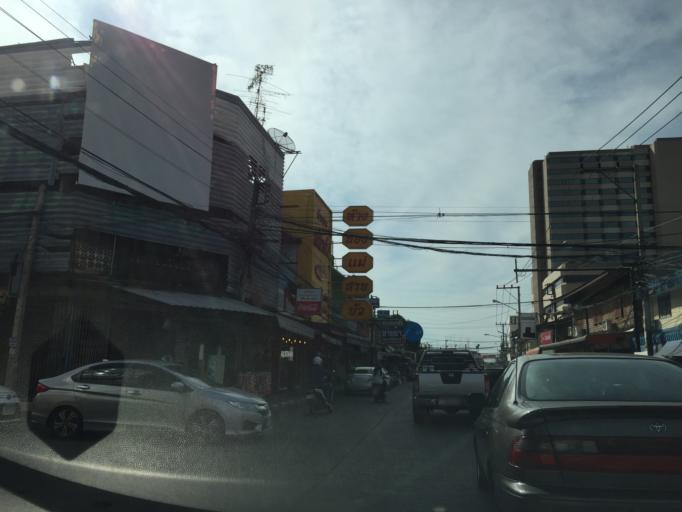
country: TH
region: Phitsanulok
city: Phitsanulok
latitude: 16.8233
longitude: 100.2651
